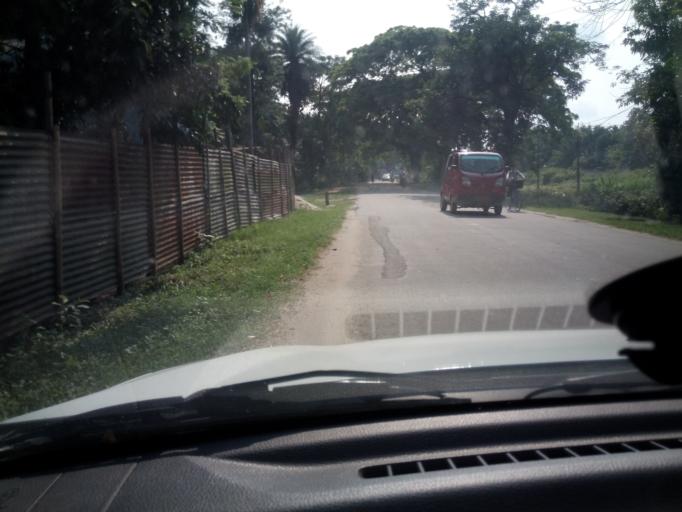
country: IN
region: Assam
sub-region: Udalguri
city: Udalguri
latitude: 26.7456
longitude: 92.1141
